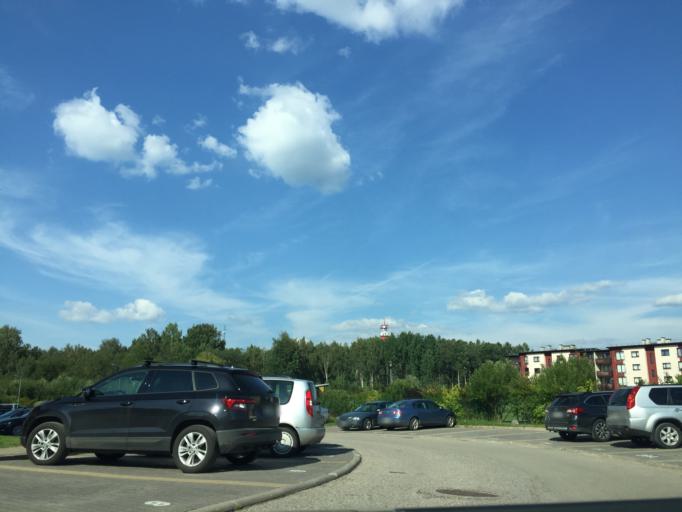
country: LV
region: Sigulda
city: Sigulda
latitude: 57.1591
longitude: 24.8706
